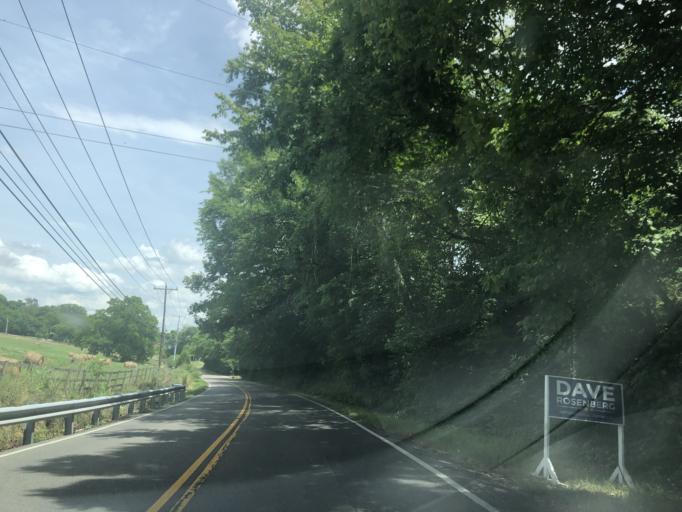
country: US
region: Tennessee
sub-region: Cheatham County
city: Pegram
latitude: 36.0552
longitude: -86.9605
